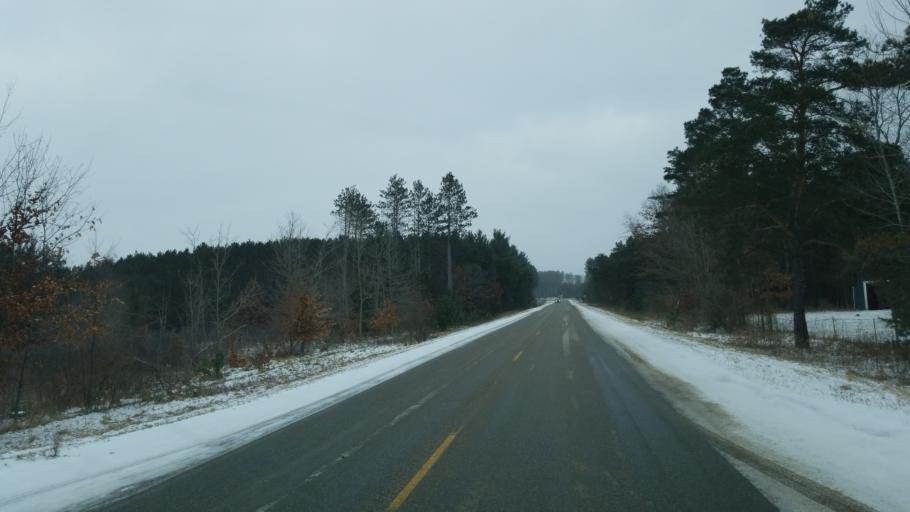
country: US
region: Michigan
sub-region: Osceola County
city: Evart
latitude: 43.8649
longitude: -85.3545
